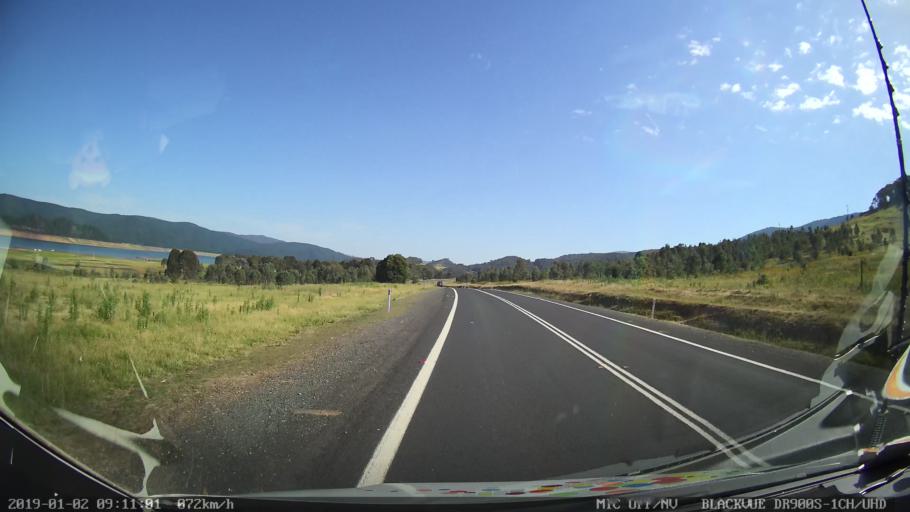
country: AU
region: New South Wales
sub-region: Tumut Shire
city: Tumut
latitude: -35.5157
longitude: 148.2688
